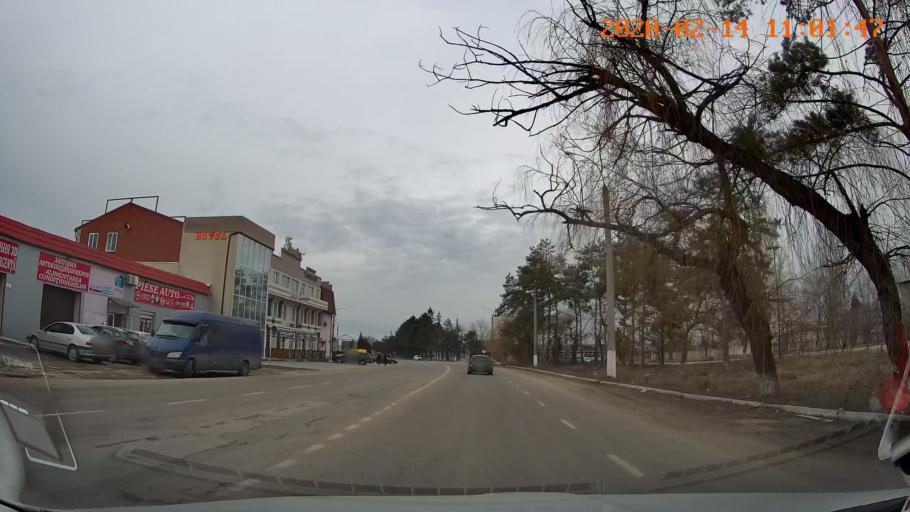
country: MD
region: Raionul Edinet
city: Edinet
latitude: 48.1618
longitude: 27.3260
